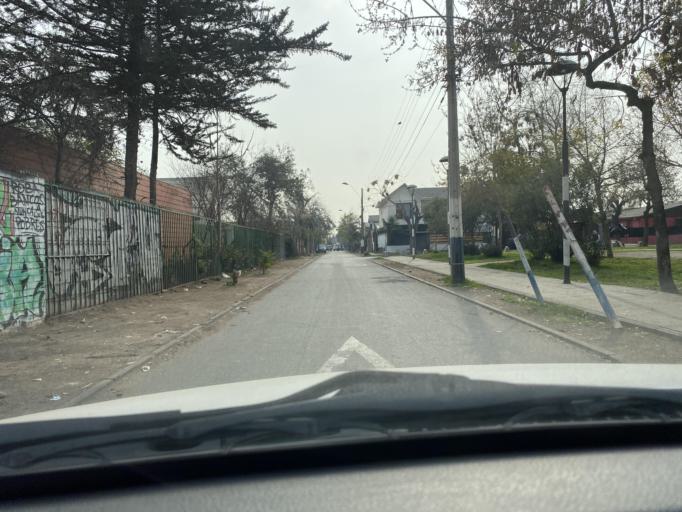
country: CL
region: Santiago Metropolitan
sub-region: Provincia de Santiago
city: La Pintana
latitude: -33.5200
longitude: -70.6256
